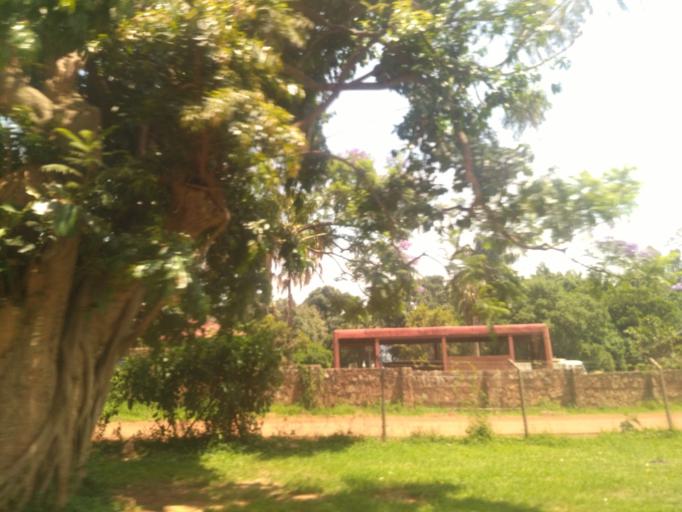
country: UG
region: Central Region
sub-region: Wakiso District
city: Entebbe
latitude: 0.0553
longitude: 32.4792
